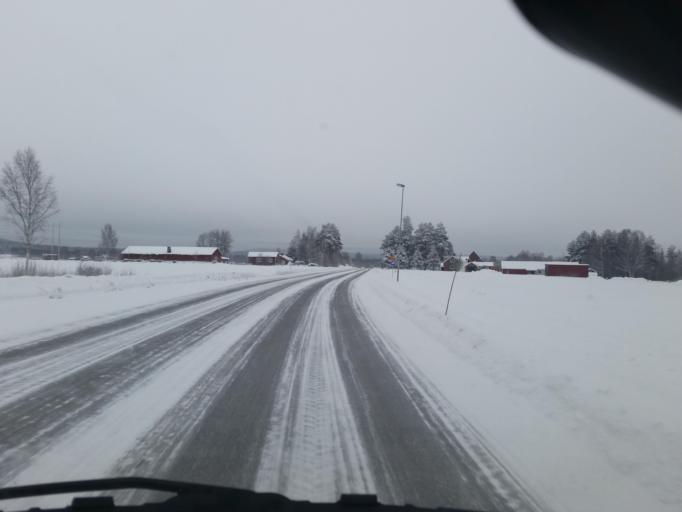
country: SE
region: Norrbotten
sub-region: Pitea Kommun
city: Roknas
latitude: 65.4447
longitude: 21.2586
